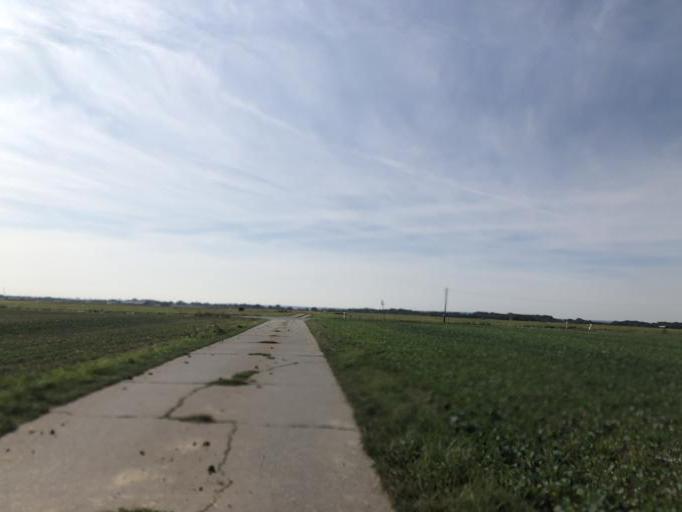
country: DE
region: Bavaria
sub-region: Regierungsbezirk Mittelfranken
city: Obermichelbach
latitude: 49.5417
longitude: 10.9489
